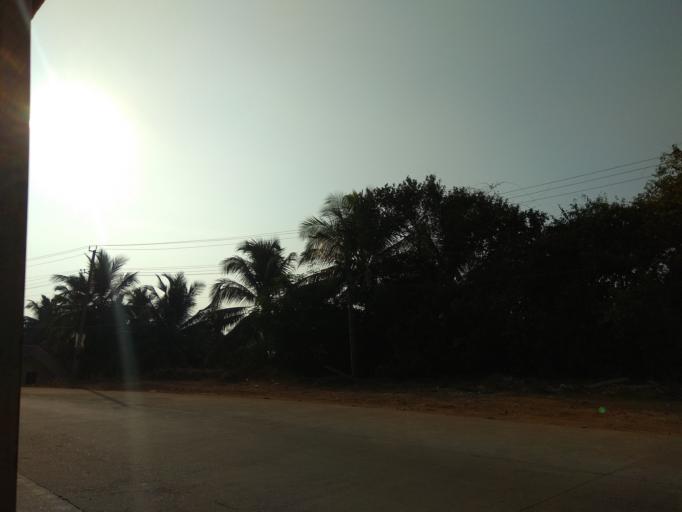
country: IN
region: Karnataka
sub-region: Dakshina Kannada
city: Mangalore
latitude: 12.9166
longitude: 74.8565
